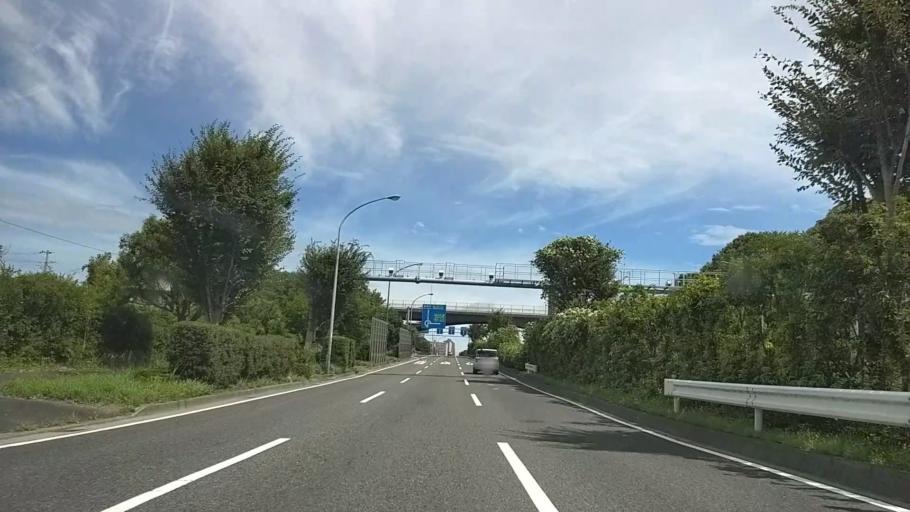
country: JP
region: Kanagawa
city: Yokohama
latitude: 35.4393
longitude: 139.5602
